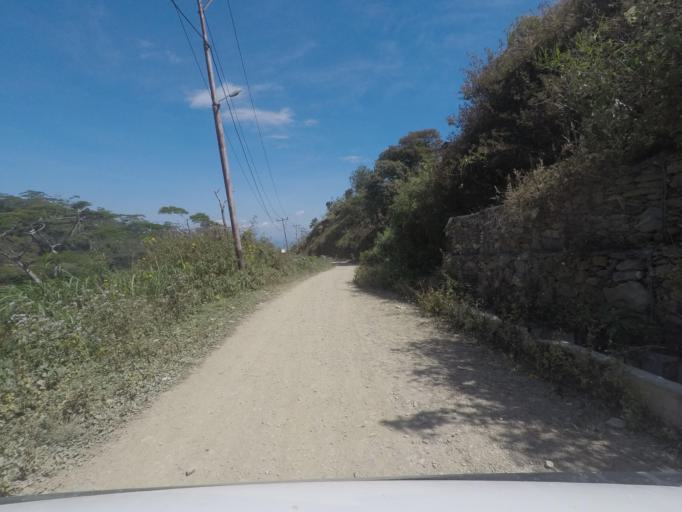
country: TL
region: Ermera
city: Gleno
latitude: -8.7529
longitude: 125.3270
